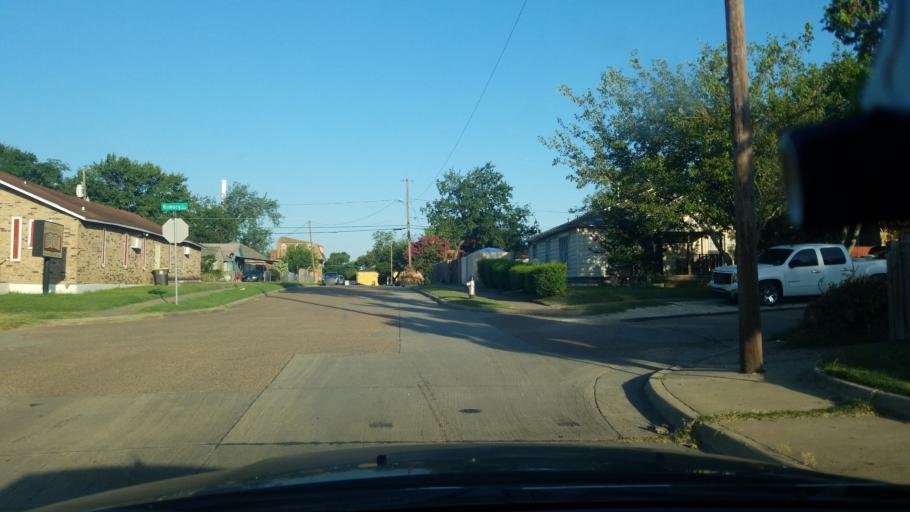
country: US
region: Texas
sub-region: Dallas County
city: Dallas
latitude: 32.7192
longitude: -96.8204
